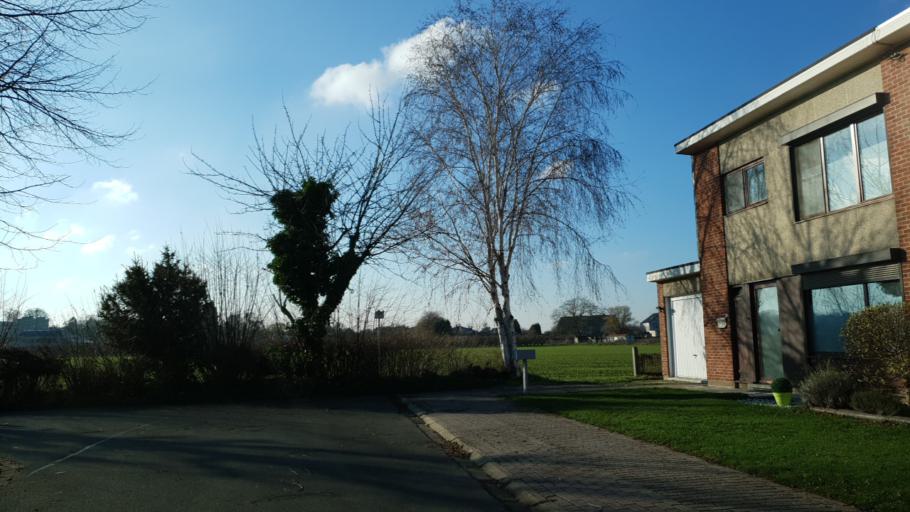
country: BE
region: Flanders
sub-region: Provincie Vlaams-Brabant
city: Herent
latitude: 50.9109
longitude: 4.6882
